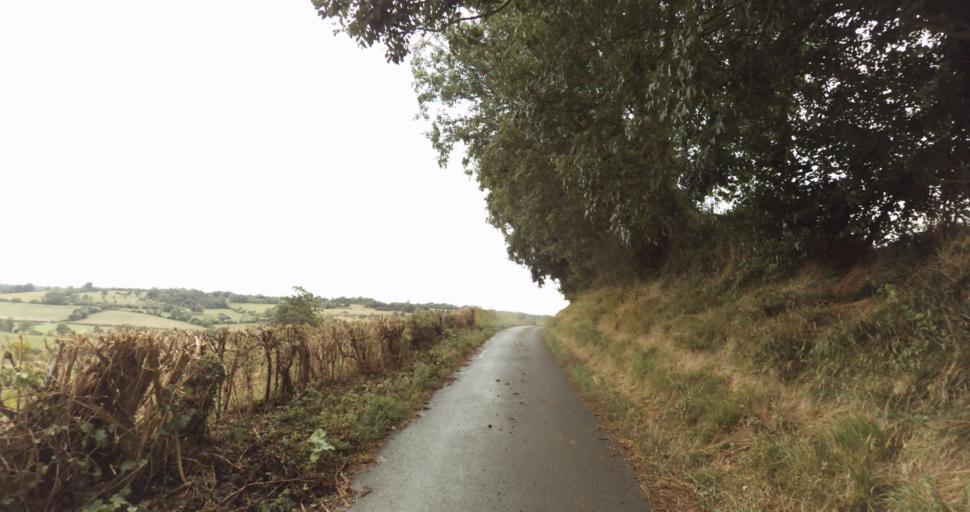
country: FR
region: Lower Normandy
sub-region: Departement de l'Orne
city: Vimoutiers
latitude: 48.8592
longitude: 0.2322
